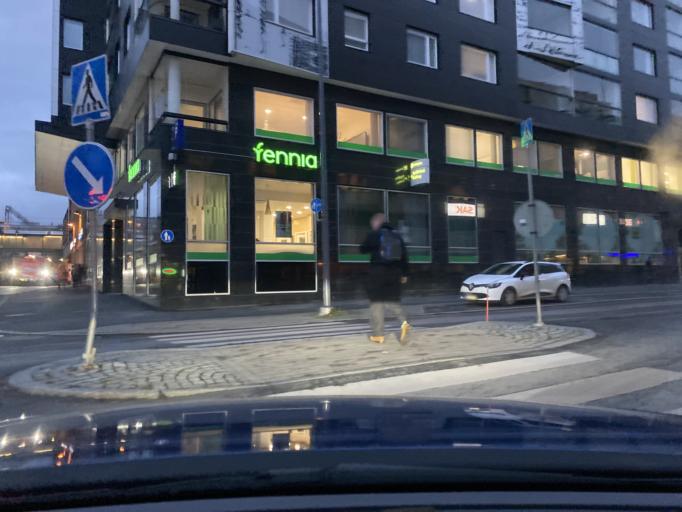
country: FI
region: Pirkanmaa
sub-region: Tampere
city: Tampere
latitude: 61.5004
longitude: 23.7710
